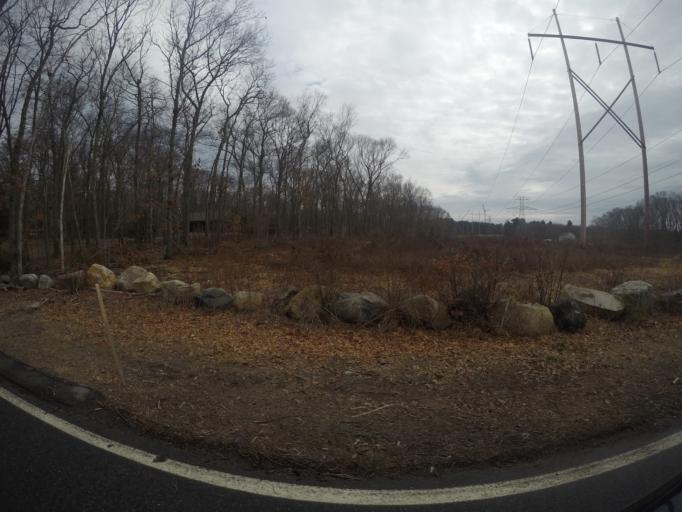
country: US
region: Massachusetts
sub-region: Bristol County
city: Easton
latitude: 42.0510
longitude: -71.1623
